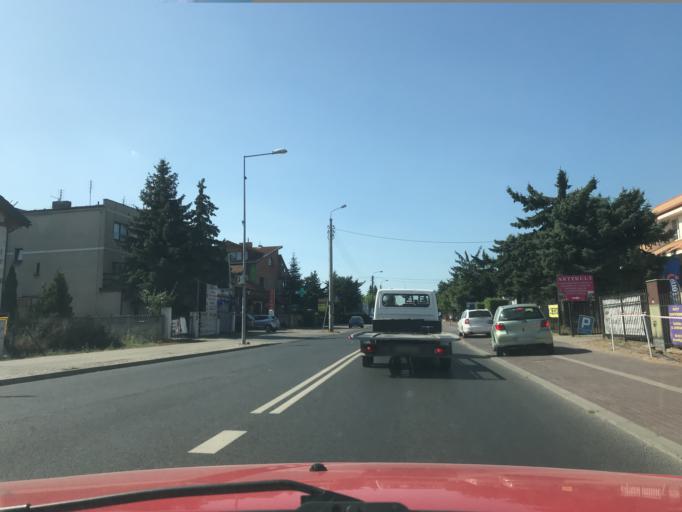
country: PL
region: Greater Poland Voivodeship
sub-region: Powiat poznanski
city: Plewiska
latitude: 52.3820
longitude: 16.8315
